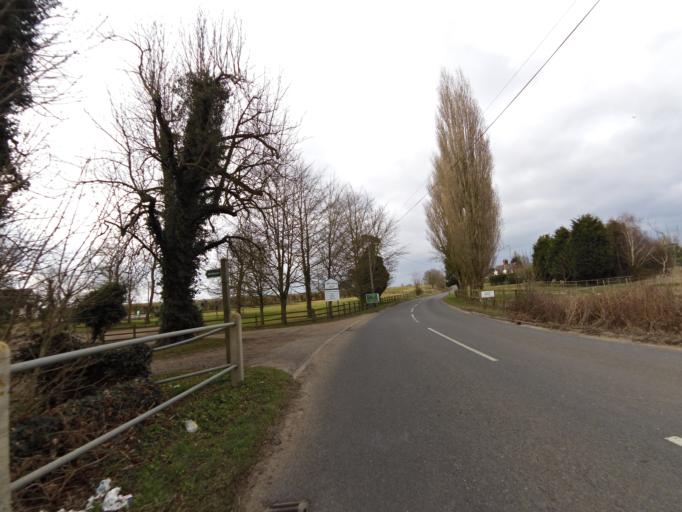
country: GB
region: England
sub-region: Suffolk
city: Ipswich
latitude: 52.1015
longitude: 1.1516
